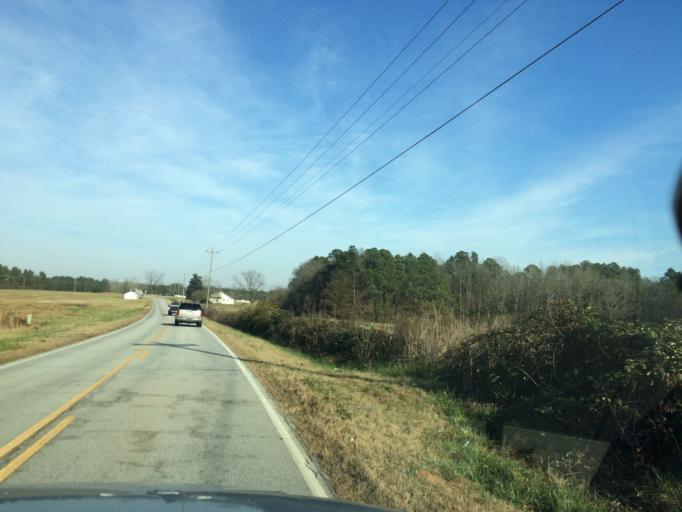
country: US
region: Georgia
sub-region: Hart County
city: Reed Creek
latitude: 34.4346
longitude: -82.9607
